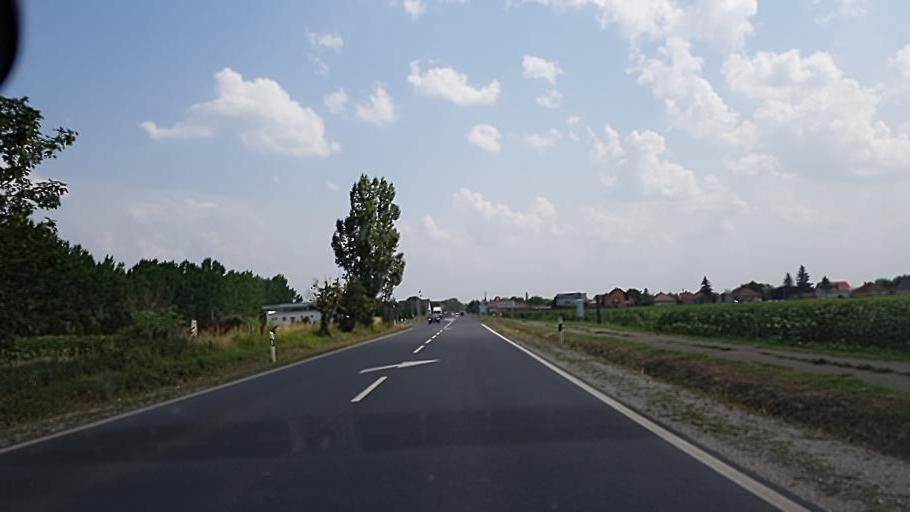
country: HU
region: Heves
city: Besenyotelek
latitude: 47.7119
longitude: 20.4238
